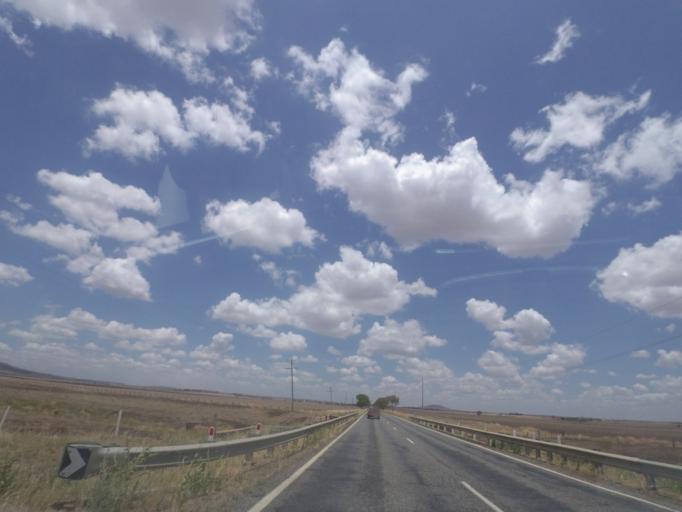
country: AU
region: Queensland
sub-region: Toowoomba
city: Top Camp
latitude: -27.9130
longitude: 151.9802
